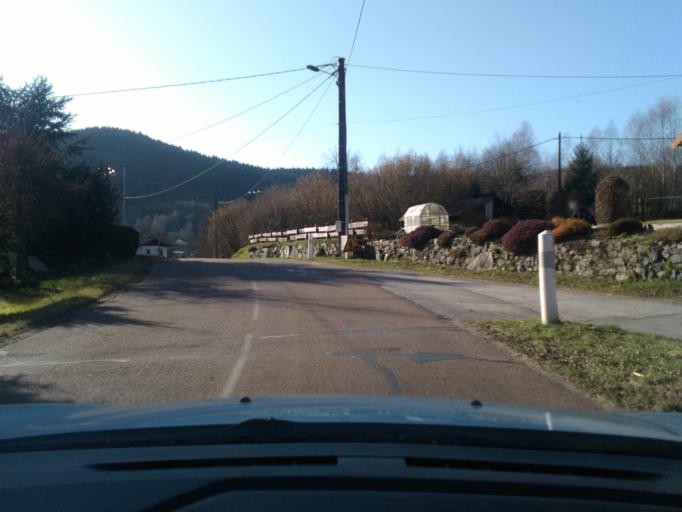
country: FR
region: Lorraine
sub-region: Departement des Vosges
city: Vecoux
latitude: 47.9832
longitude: 6.6304
